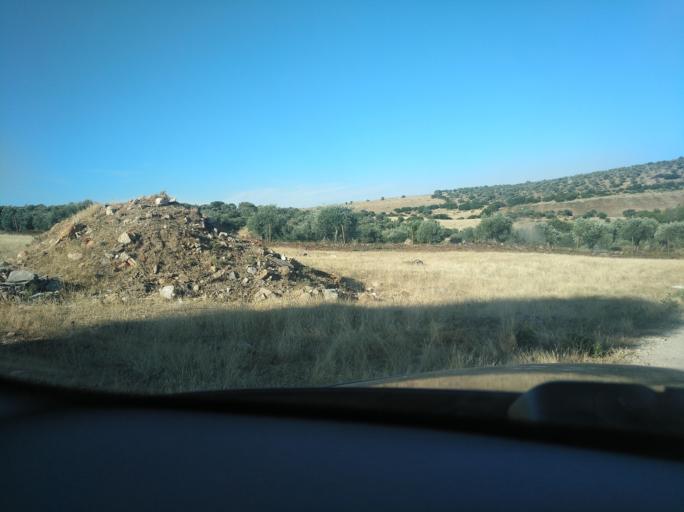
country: PT
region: Portalegre
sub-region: Elvas
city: Elvas
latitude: 38.8634
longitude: -7.1547
